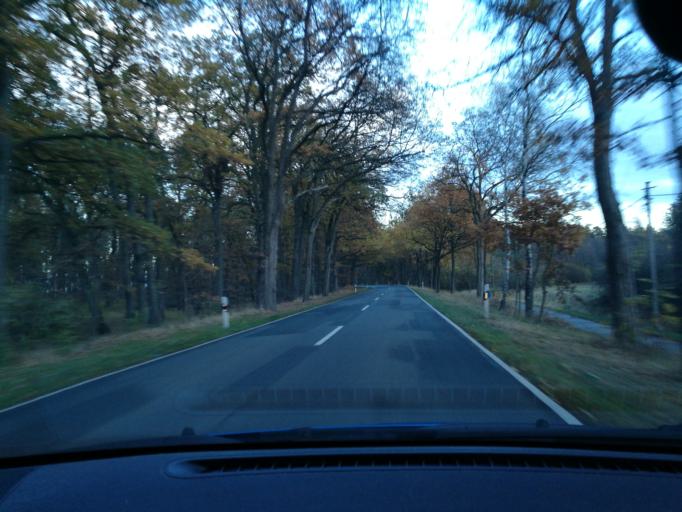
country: DE
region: Lower Saxony
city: Gartow
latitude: 53.0343
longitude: 11.4168
